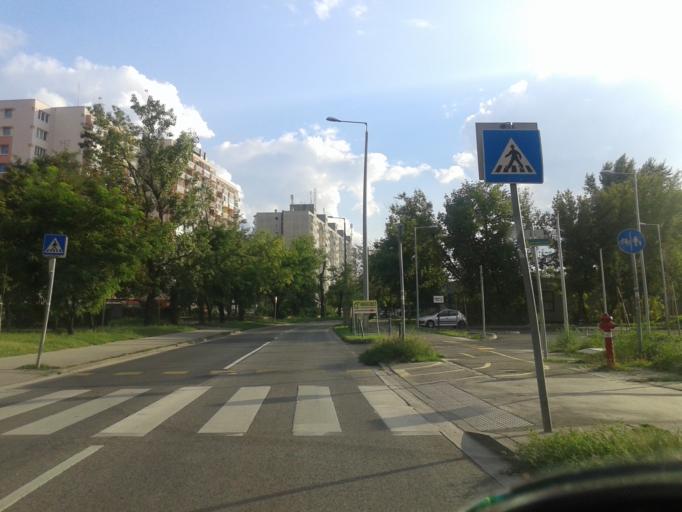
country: HU
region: Budapest
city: Budapest XXI. keruelet
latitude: 47.4208
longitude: 19.0675
